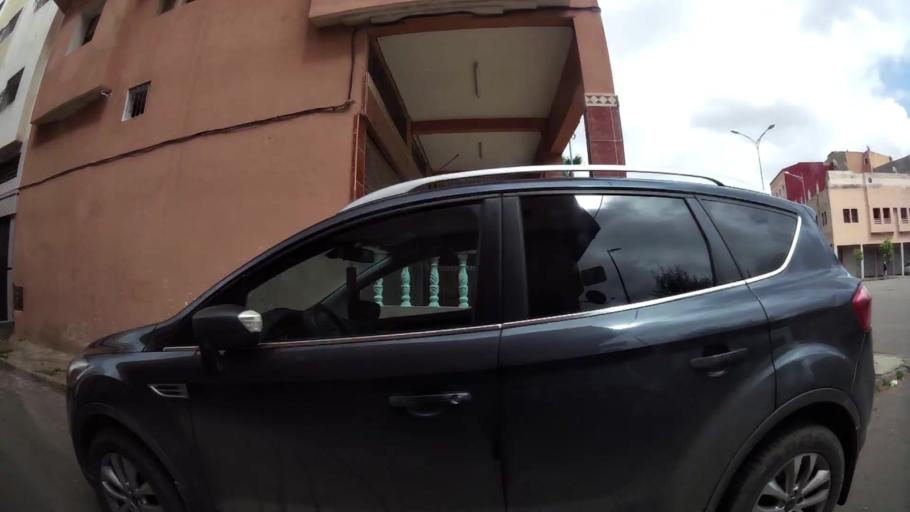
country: MA
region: Grand Casablanca
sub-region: Casablanca
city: Casablanca
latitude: 33.5309
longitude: -7.6096
